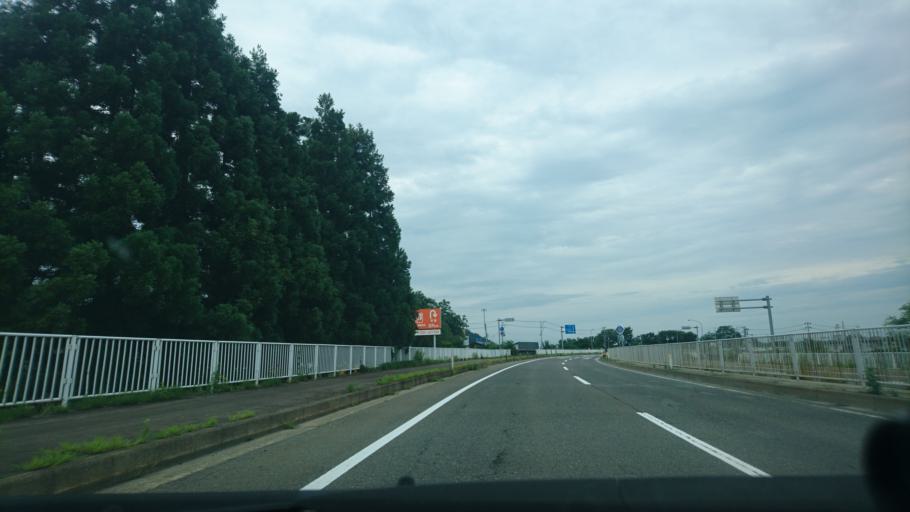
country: JP
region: Akita
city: Omagari
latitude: 39.4781
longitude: 140.4601
